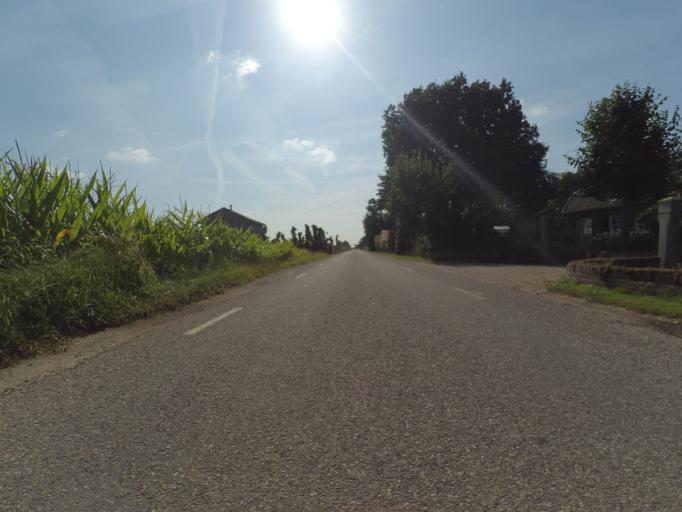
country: NL
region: Utrecht
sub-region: Gemeente Utrechtse Heuvelrug
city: Driebergen-Rijsenburg
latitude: 51.9999
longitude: 5.2875
